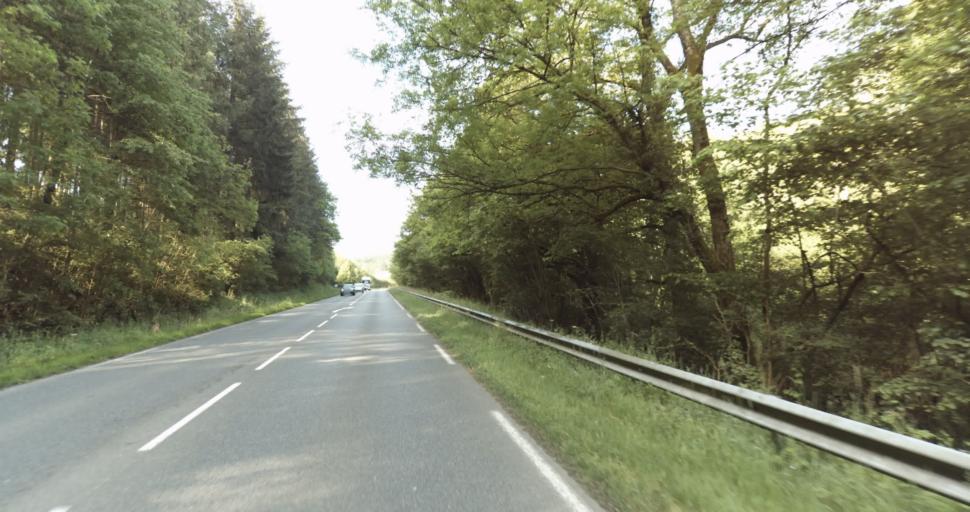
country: FR
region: Limousin
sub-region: Departement de la Haute-Vienne
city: Le Vigen
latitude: 45.7423
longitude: 1.2854
